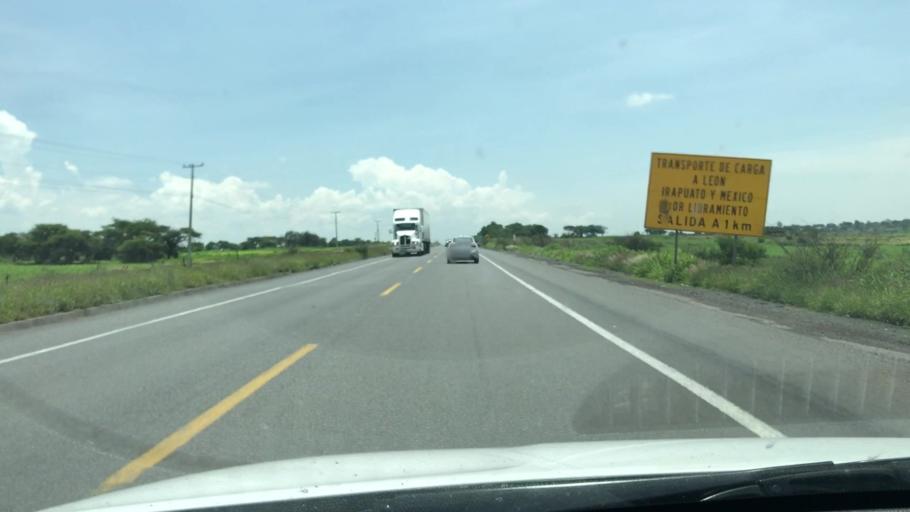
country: MX
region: Jalisco
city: Degollado
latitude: 20.3641
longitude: -102.1390
